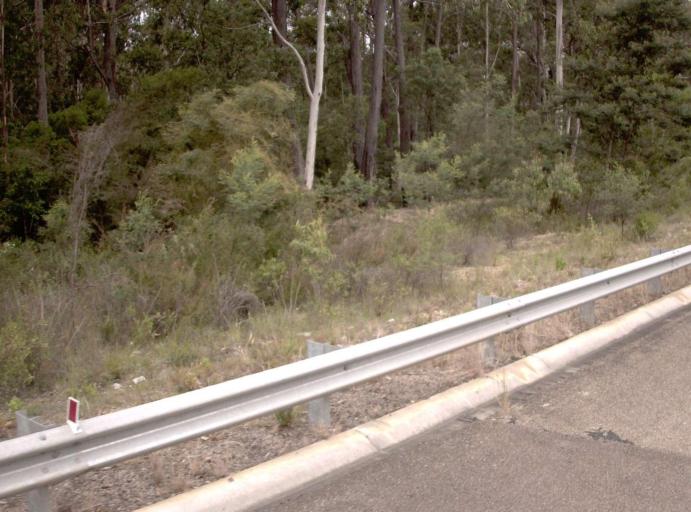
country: AU
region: Victoria
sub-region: East Gippsland
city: Lakes Entrance
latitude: -37.7200
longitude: 148.0798
